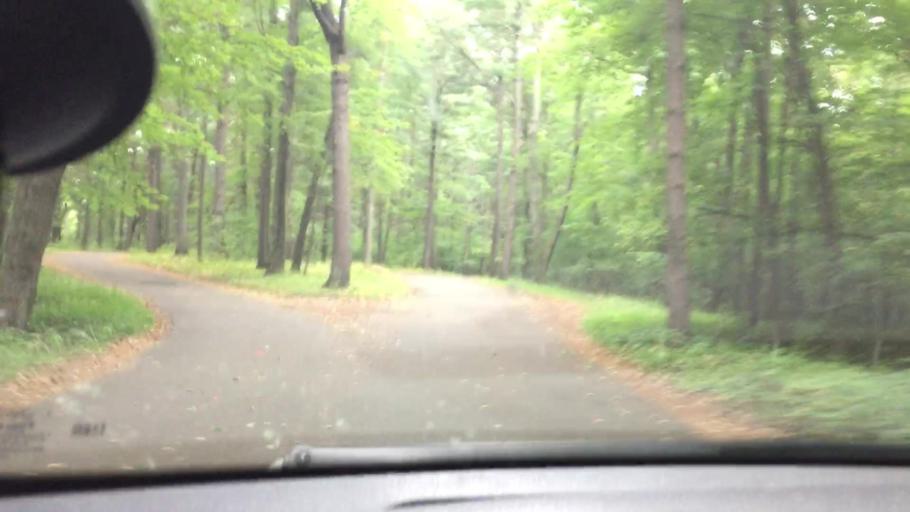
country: US
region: Wisconsin
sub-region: Chippewa County
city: Chippewa Falls
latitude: 44.9598
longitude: -91.4015
